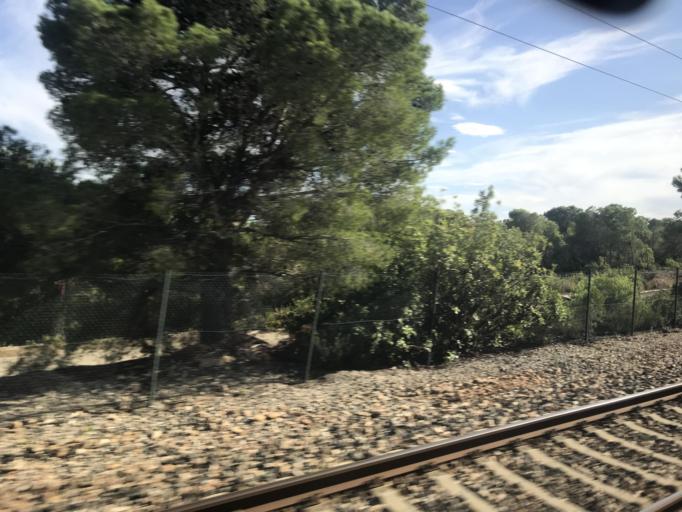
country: ES
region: Catalonia
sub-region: Provincia de Tarragona
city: l'Ametlla de Mar
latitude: 40.8577
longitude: 0.7682
